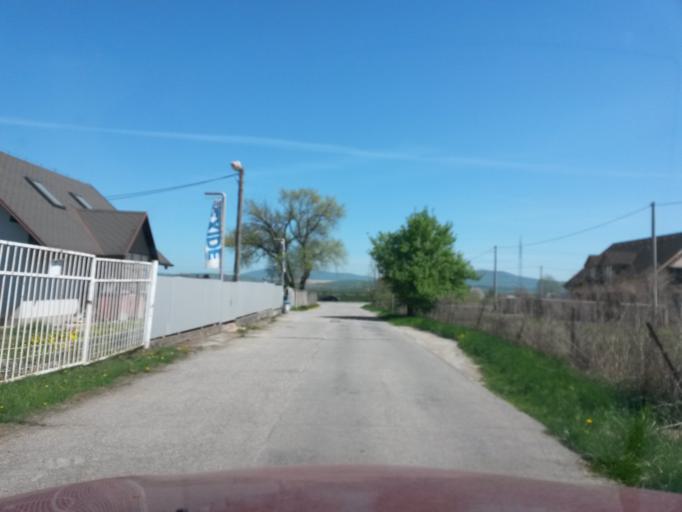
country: SK
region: Kosicky
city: Kosice
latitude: 48.6576
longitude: 21.2693
